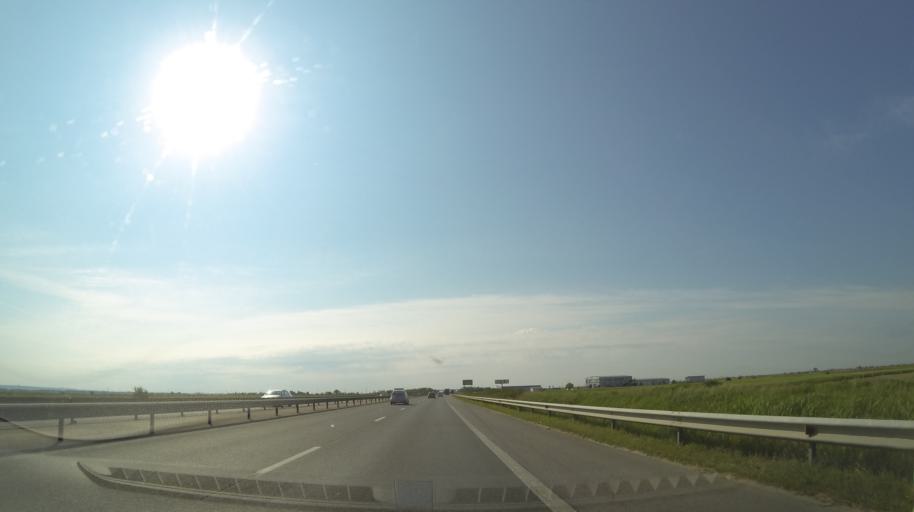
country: RO
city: Oarja Sat
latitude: 44.7922
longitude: 24.9861
